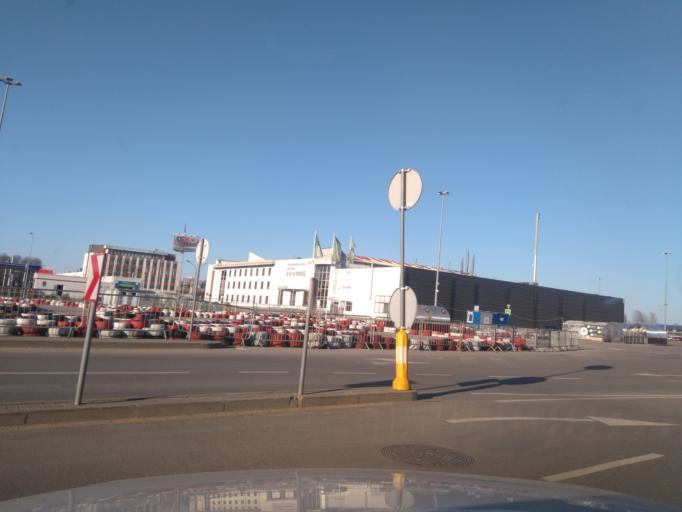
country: LT
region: Kauno apskritis
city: Dainava (Kaunas)
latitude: 54.9090
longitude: 23.9830
